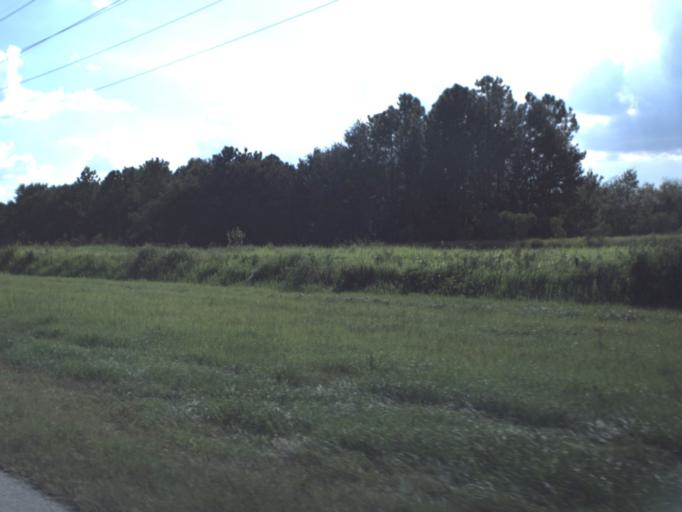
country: US
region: Florida
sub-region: Polk County
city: Mulberry
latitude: 27.7813
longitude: -81.9854
